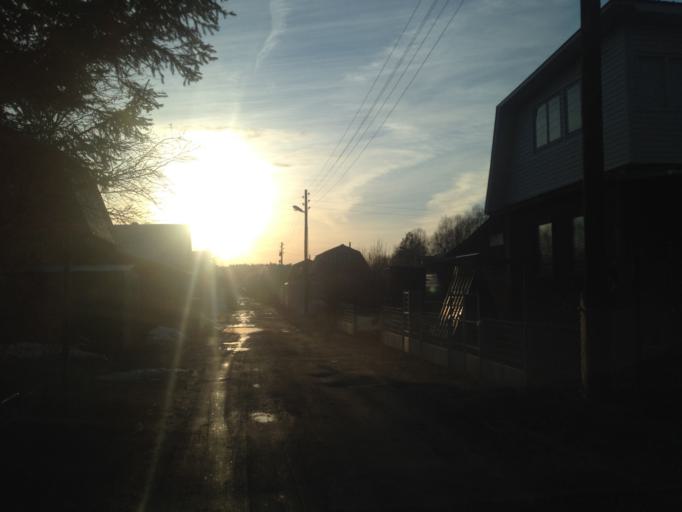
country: RU
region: Sverdlovsk
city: Shirokaya Rechka
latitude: 56.8096
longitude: 60.4286
